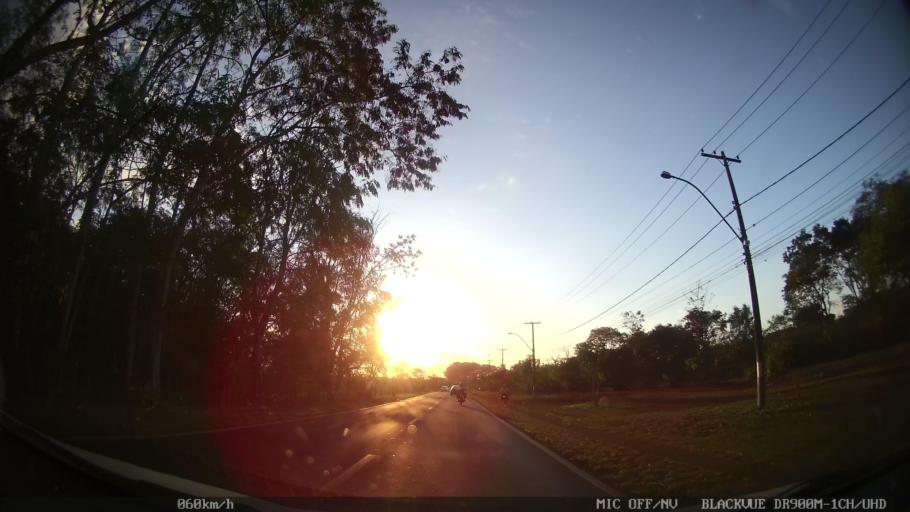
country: BR
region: Sao Paulo
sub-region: Ribeirao Preto
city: Ribeirao Preto
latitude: -21.1538
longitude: -47.7783
